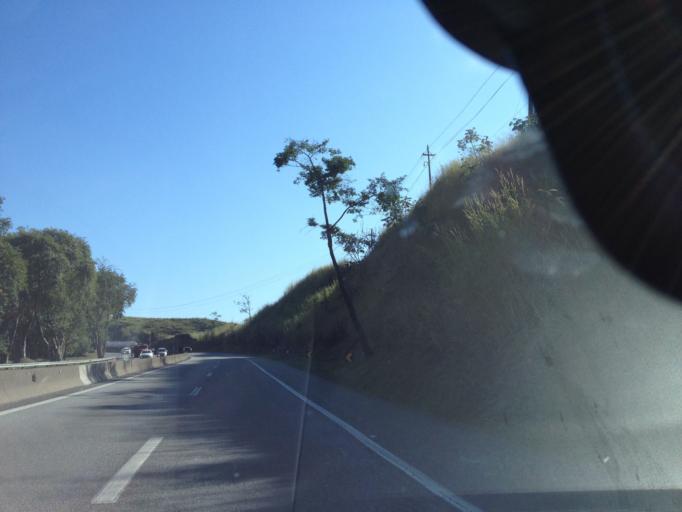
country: BR
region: Rio de Janeiro
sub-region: Porto Real
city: Porto Real
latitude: -22.4794
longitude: -44.2620
